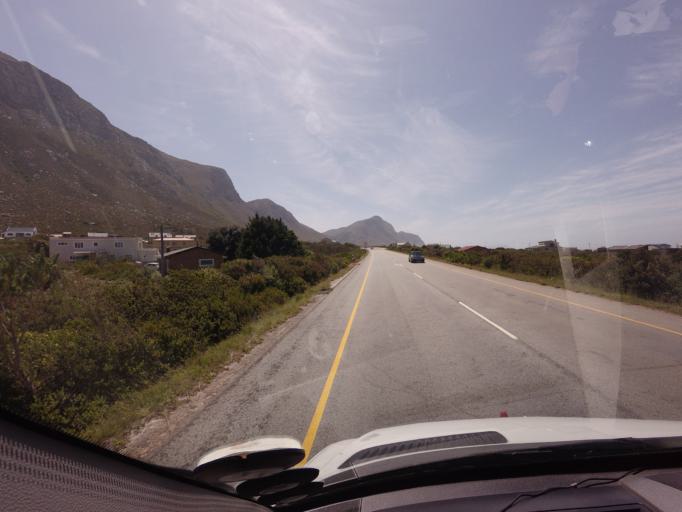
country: ZA
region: Western Cape
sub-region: Overberg District Municipality
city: Grabouw
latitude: -34.3585
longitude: 18.8899
